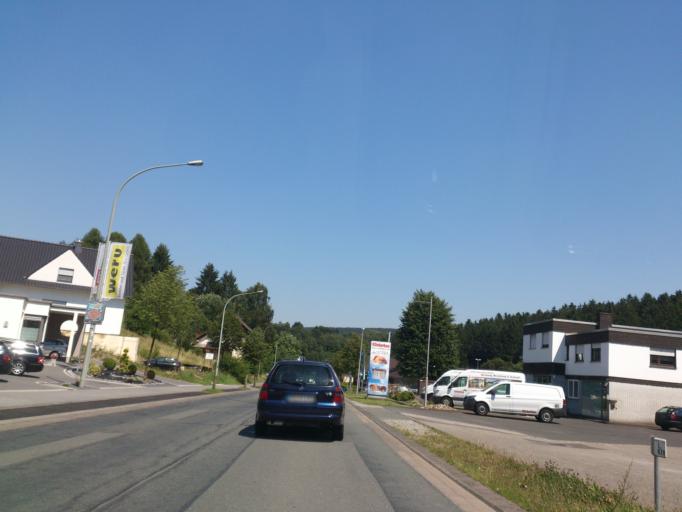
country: DE
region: North Rhine-Westphalia
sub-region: Regierungsbezirk Detmold
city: Altenbeken
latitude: 51.7544
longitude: 8.9519
